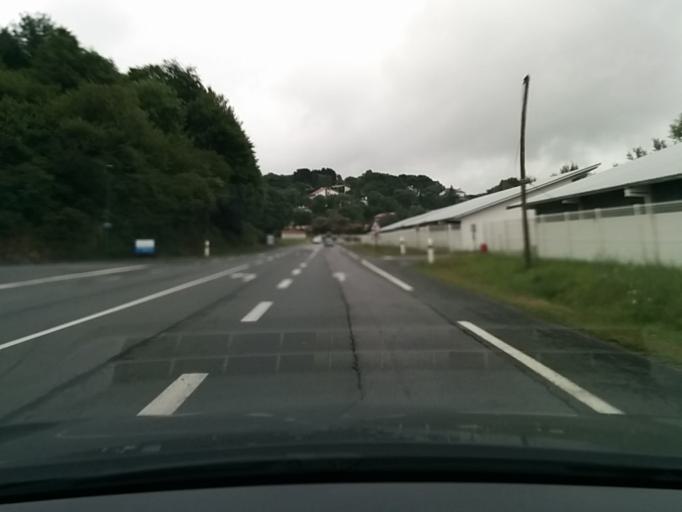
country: FR
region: Aquitaine
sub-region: Departement des Pyrenees-Atlantiques
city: Ciboure
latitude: 43.3823
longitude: -1.6914
